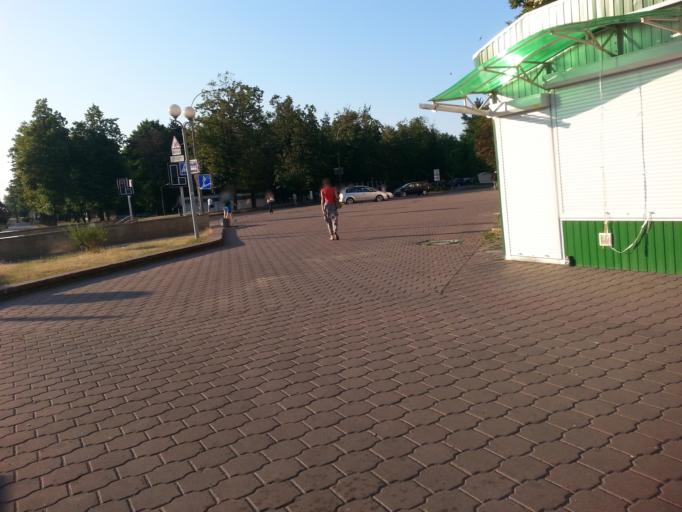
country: BY
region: Minsk
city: Vyaliki Trastsyanets
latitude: 53.8683
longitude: 27.6499
